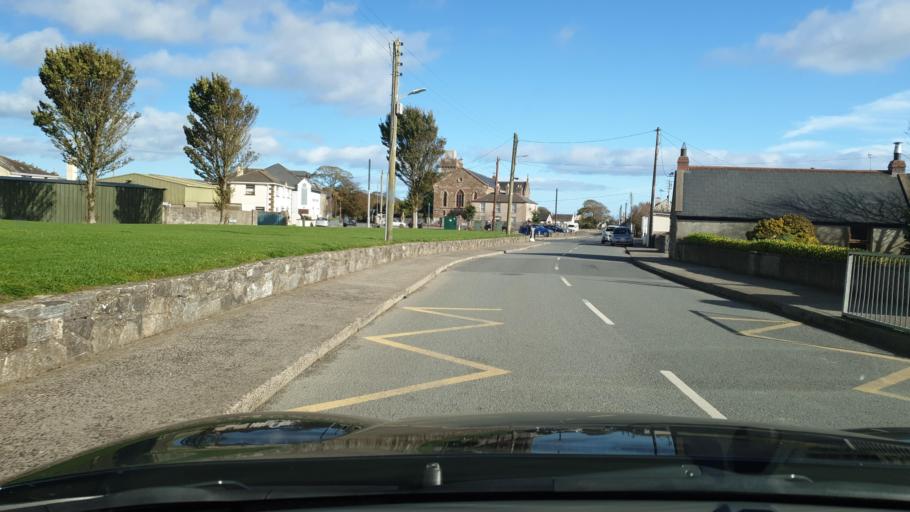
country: IE
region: Leinster
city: An Ros
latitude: 53.5211
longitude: -6.1043
